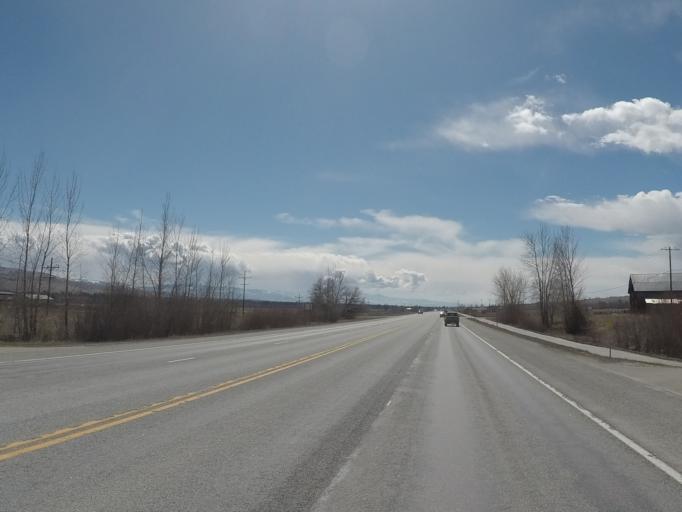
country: US
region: Montana
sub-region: Missoula County
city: Lolo
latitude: 46.7377
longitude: -114.0808
